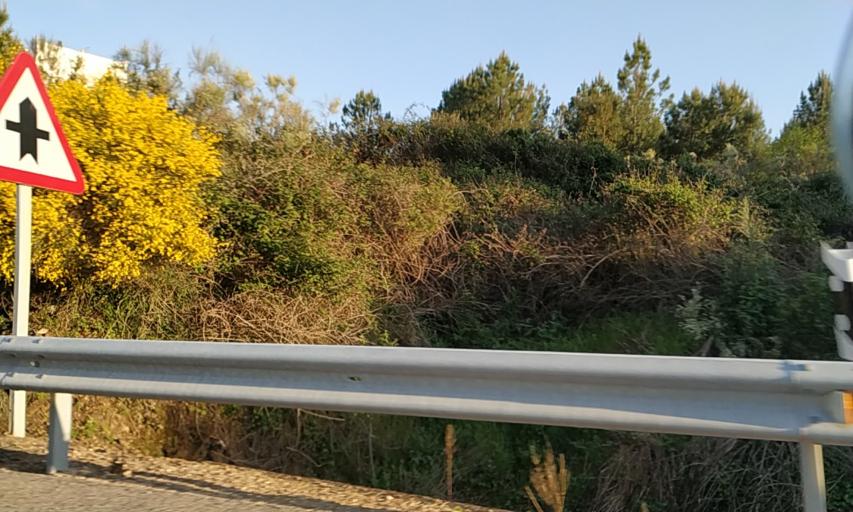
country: PT
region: Portalegre
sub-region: Portalegre
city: Sao Juliao
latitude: 39.3417
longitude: -7.2893
